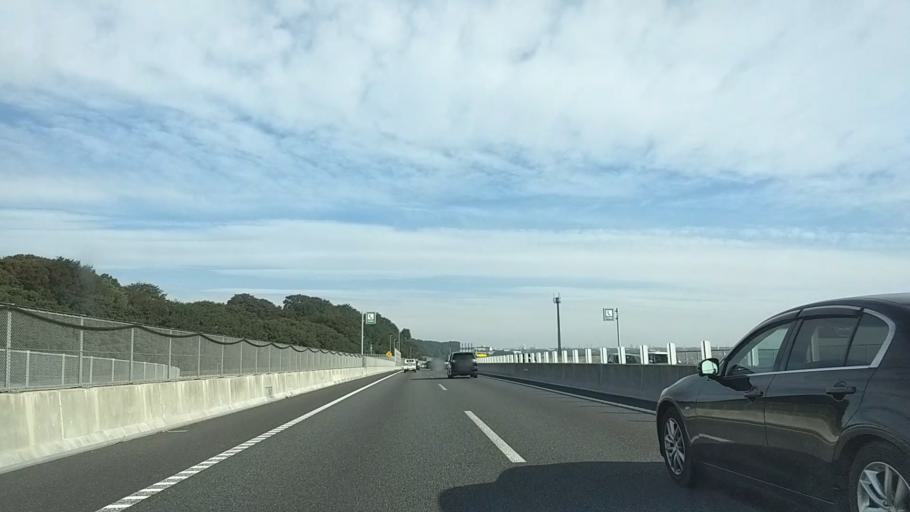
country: JP
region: Kanagawa
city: Zama
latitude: 35.4885
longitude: 139.3697
